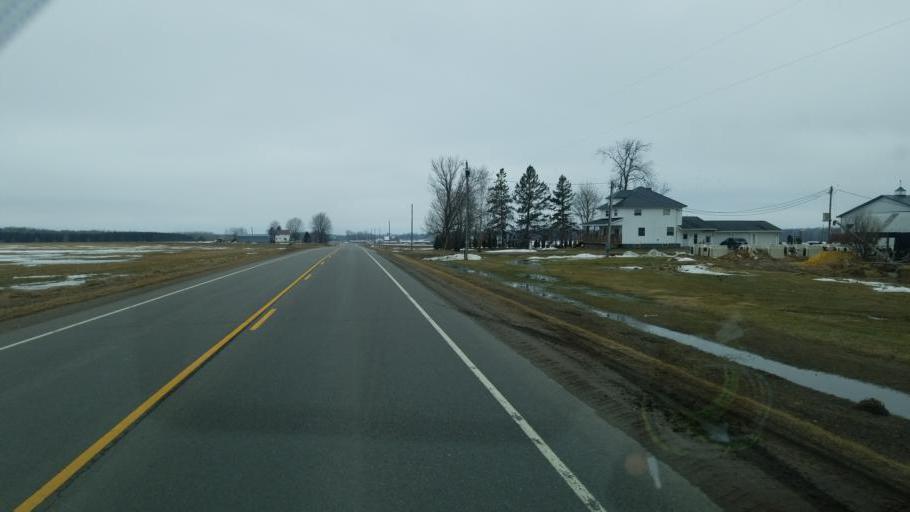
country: US
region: Wisconsin
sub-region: Marathon County
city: Spencer
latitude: 44.6562
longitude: -90.3318
